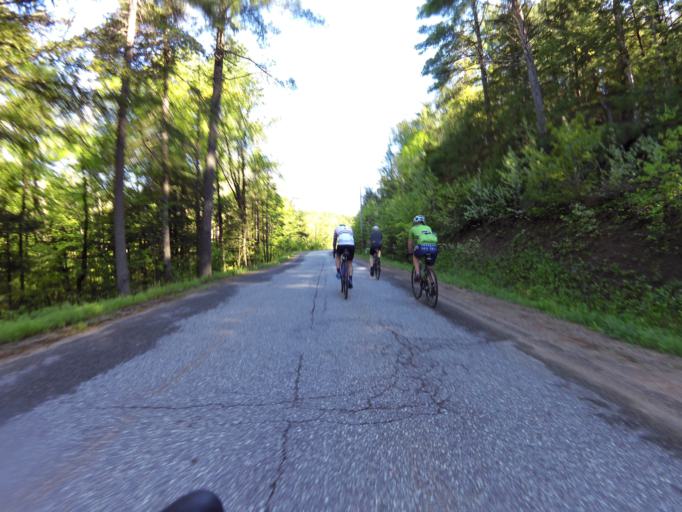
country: CA
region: Quebec
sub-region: Outaouais
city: Wakefield
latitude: 45.6158
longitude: -75.8814
